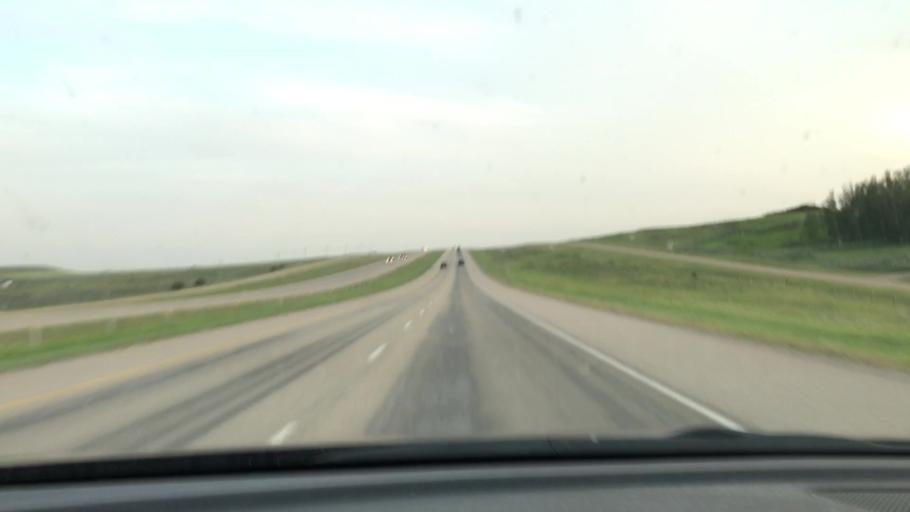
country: CA
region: Alberta
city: Carstairs
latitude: 51.5492
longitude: -114.0253
